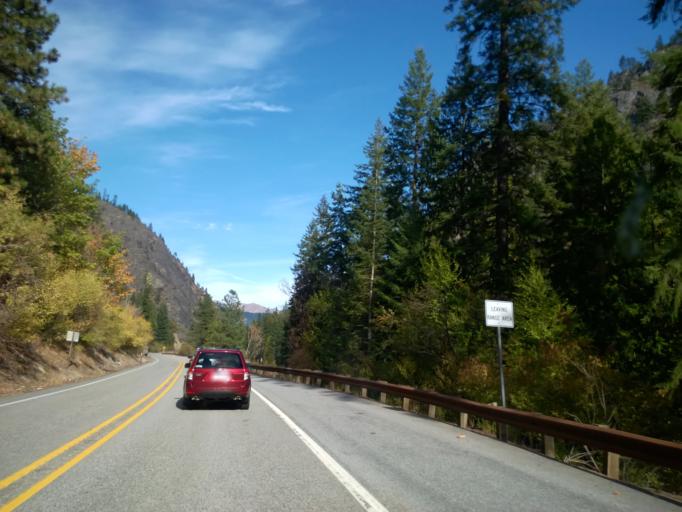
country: US
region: Washington
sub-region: Chelan County
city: Leavenworth
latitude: 47.5846
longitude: -120.6932
